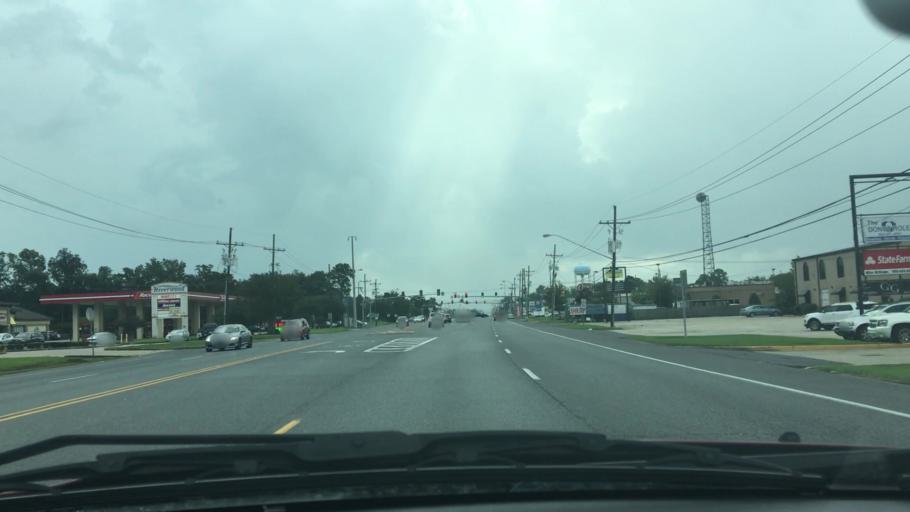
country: US
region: Louisiana
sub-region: Saint John the Baptist Parish
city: Laplace
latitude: 30.0682
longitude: -90.4832
